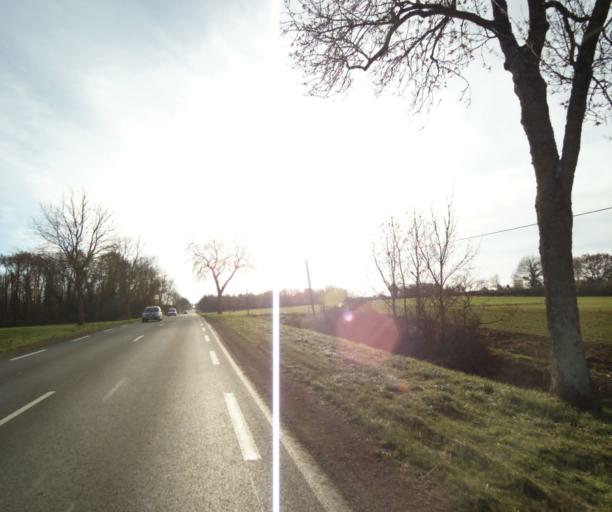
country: FR
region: Poitou-Charentes
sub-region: Departement de la Charente-Maritime
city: Saint-Hilaire-de-Villefranche
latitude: 45.8364
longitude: -0.5373
